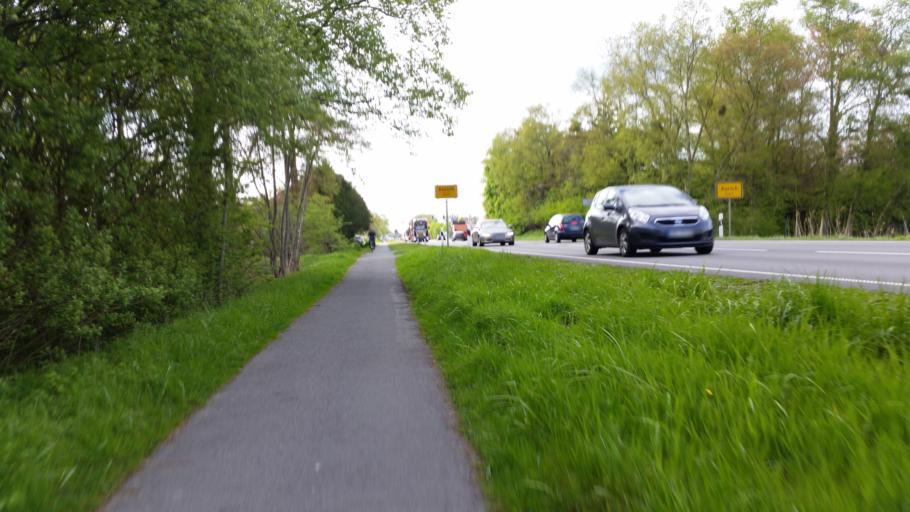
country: DE
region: Lower Saxony
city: Aurich
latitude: 53.4554
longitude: 7.4993
